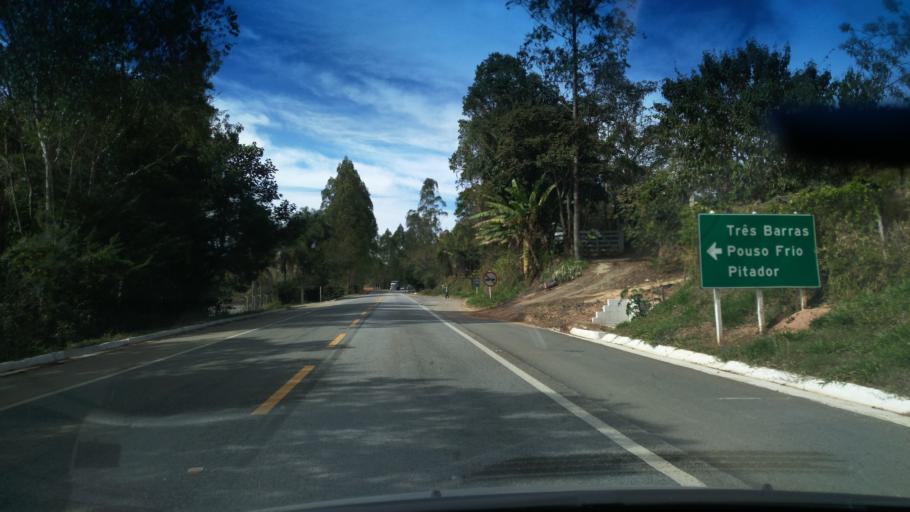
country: BR
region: Minas Gerais
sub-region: Borda Da Mata
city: Borda da Mata
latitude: -22.1411
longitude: -46.1351
